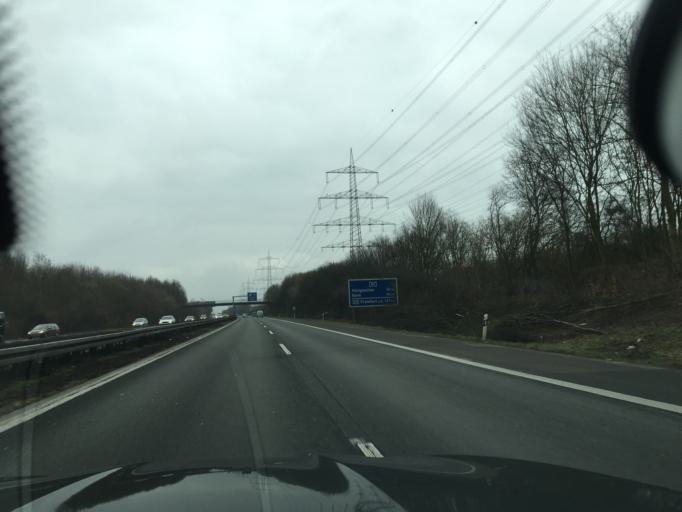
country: DE
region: North Rhine-Westphalia
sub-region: Regierungsbezirk Koln
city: Troisdorf
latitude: 50.8175
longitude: 7.1125
